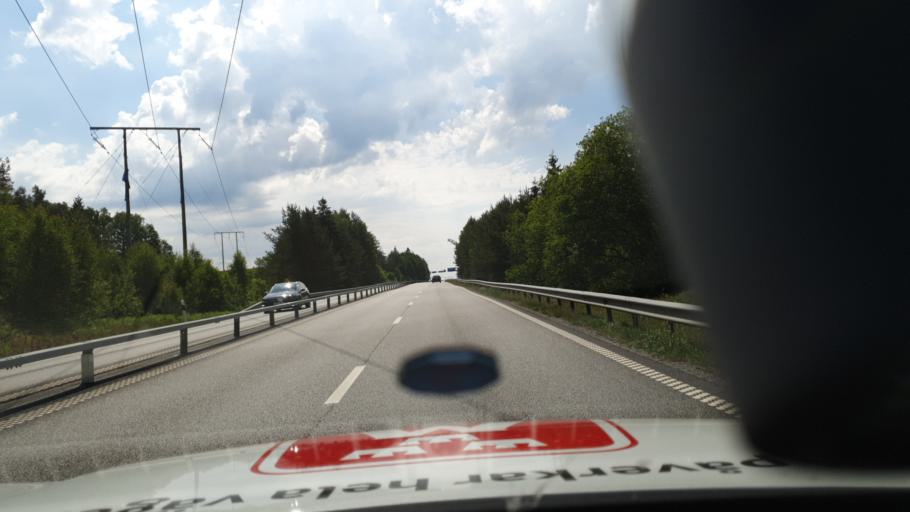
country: SE
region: Joenkoeping
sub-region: Jonkopings Kommun
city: Bankeryd
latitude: 57.7970
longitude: 14.0979
